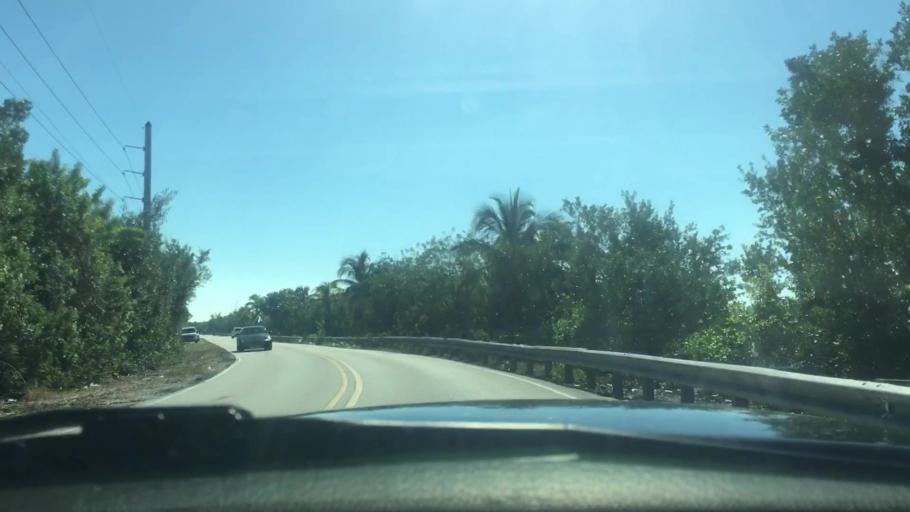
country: US
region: Florida
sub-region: Monroe County
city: North Key Largo
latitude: 25.2970
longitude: -80.3857
